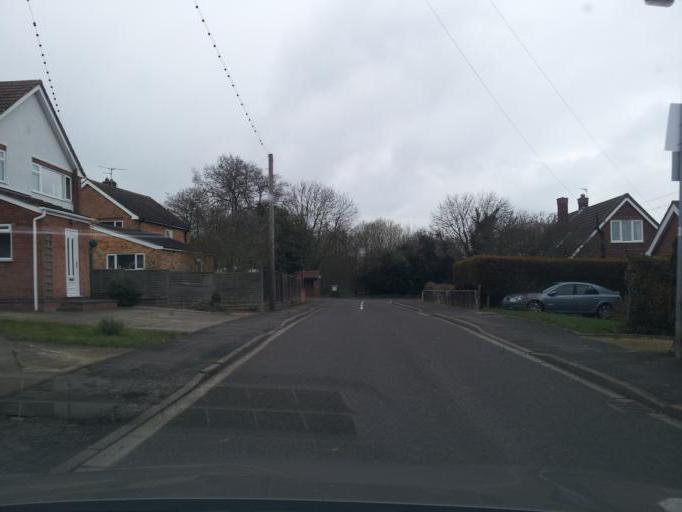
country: GB
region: England
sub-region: Lincolnshire
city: Barrowby
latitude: 52.9167
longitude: -0.6840
